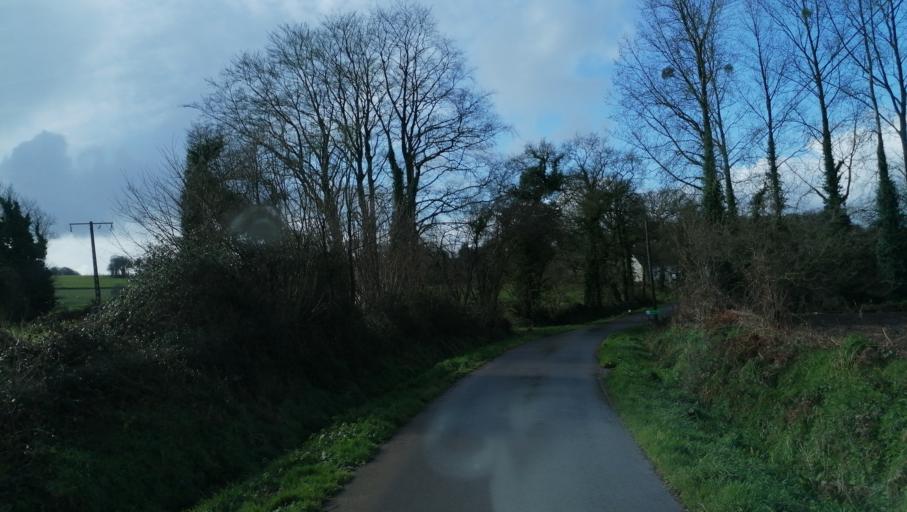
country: FR
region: Brittany
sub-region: Departement des Cotes-d'Armor
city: Lanrodec
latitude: 48.4944
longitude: -3.0243
